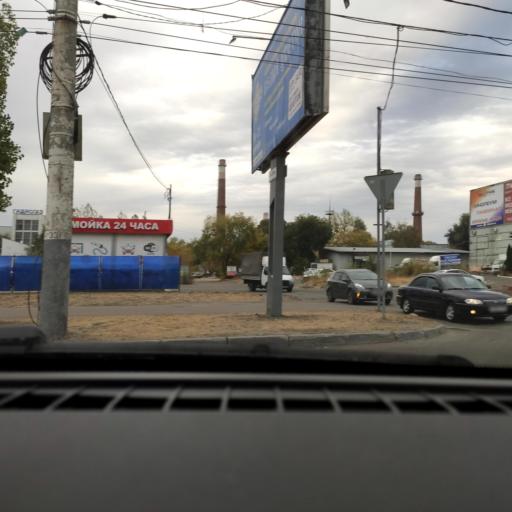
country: RU
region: Voronezj
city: Voronezh
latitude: 51.6897
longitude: 39.2668
